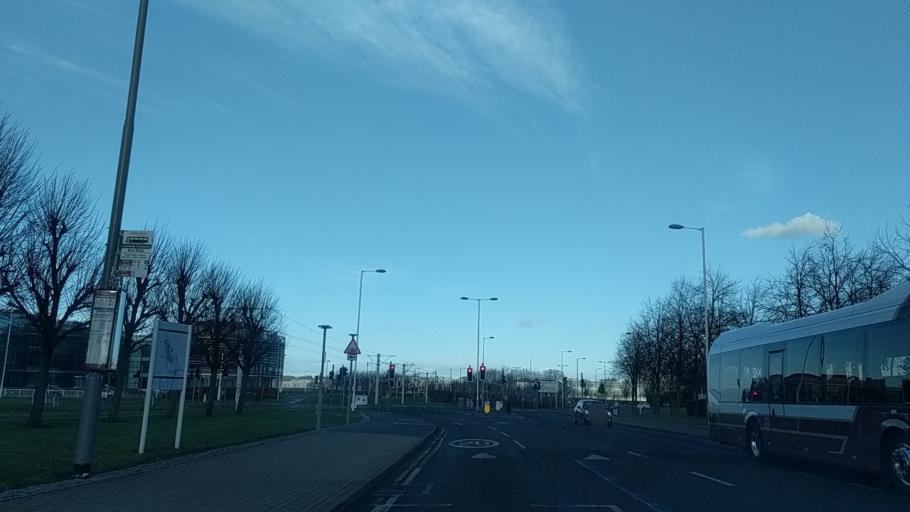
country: GB
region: Scotland
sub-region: Edinburgh
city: Currie
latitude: 55.9347
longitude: -3.3161
